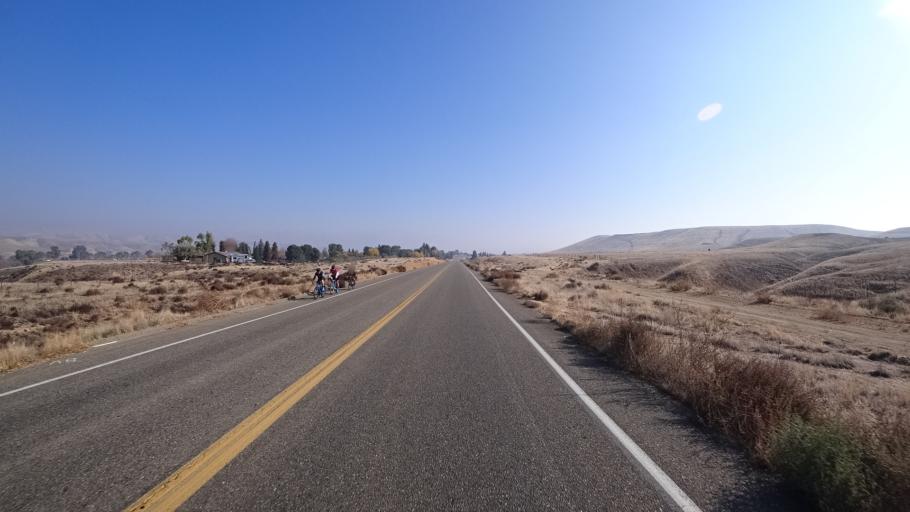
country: US
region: California
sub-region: Kern County
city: Oildale
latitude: 35.4305
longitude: -118.8799
